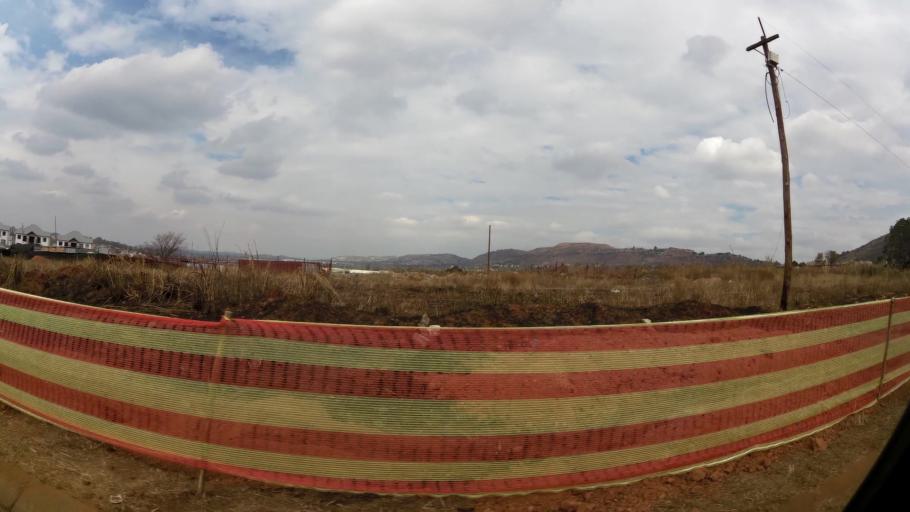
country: ZA
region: Gauteng
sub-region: City of Johannesburg Metropolitan Municipality
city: Roodepoort
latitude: -26.1024
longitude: 27.8817
